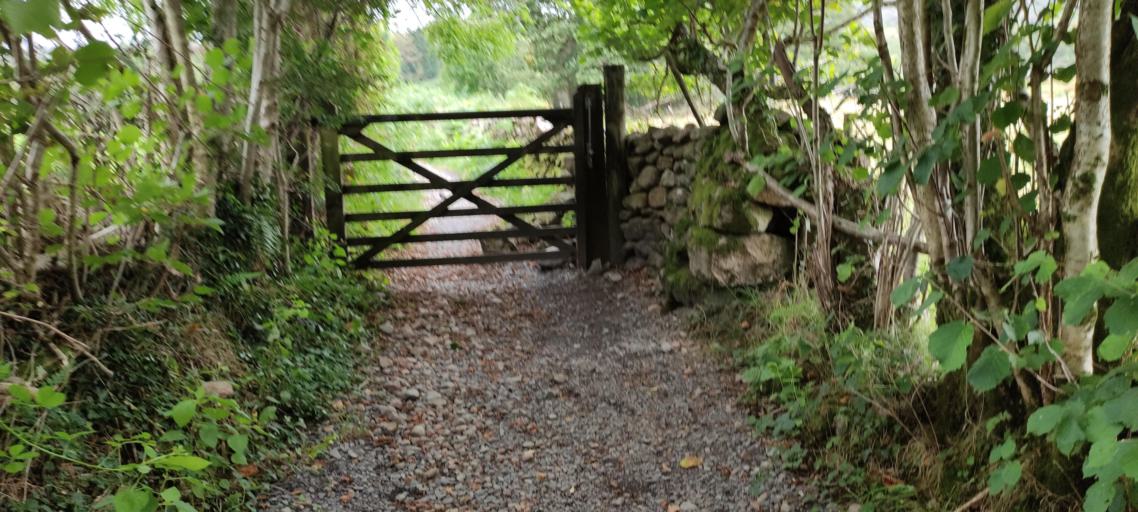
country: GB
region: England
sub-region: Cumbria
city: Millom
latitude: 54.3930
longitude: -3.2745
